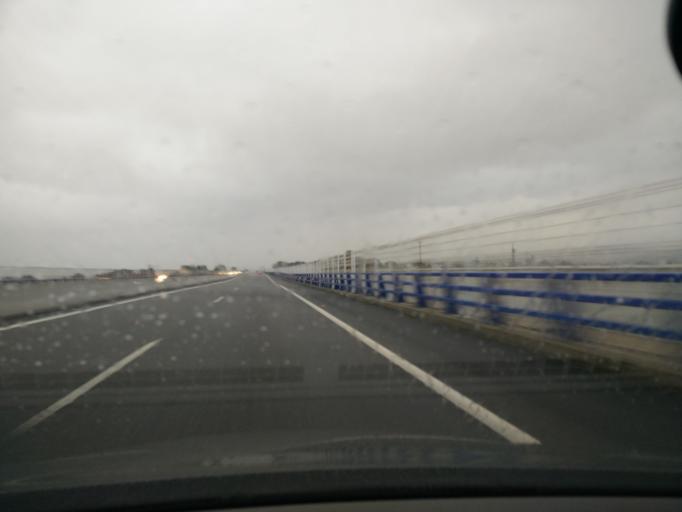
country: ES
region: Galicia
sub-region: Provincia de Lugo
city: Ribadeo
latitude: 43.5428
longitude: -7.0372
